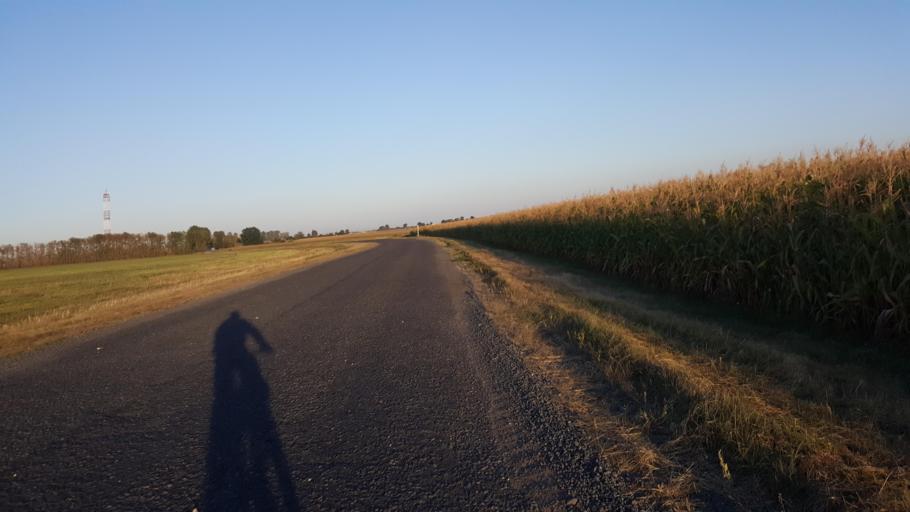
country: BY
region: Brest
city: Vysokaye
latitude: 52.2976
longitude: 23.5032
